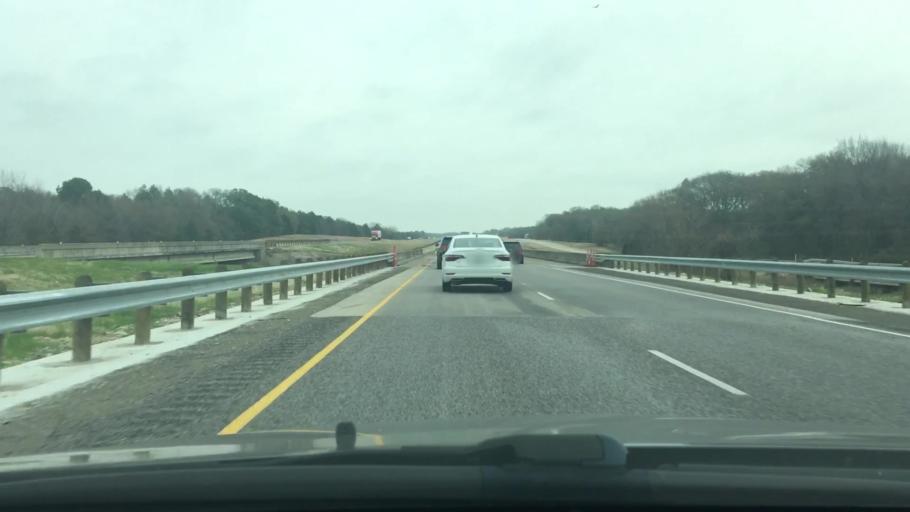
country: US
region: Texas
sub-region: Freestone County
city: Fairfield
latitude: 31.7500
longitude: -96.1996
